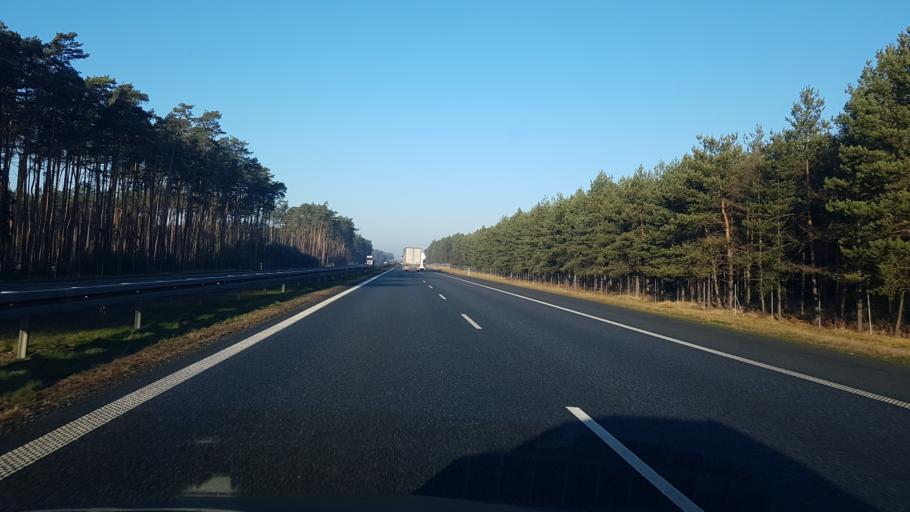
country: PL
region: Opole Voivodeship
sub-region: Powiat opolski
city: Komprachcice
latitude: 50.6078
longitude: 17.7819
